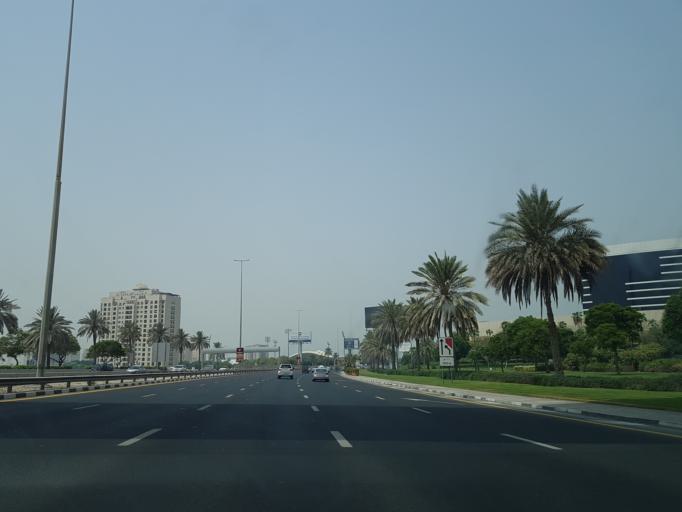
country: AE
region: Ash Shariqah
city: Sharjah
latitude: 25.2277
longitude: 55.3316
